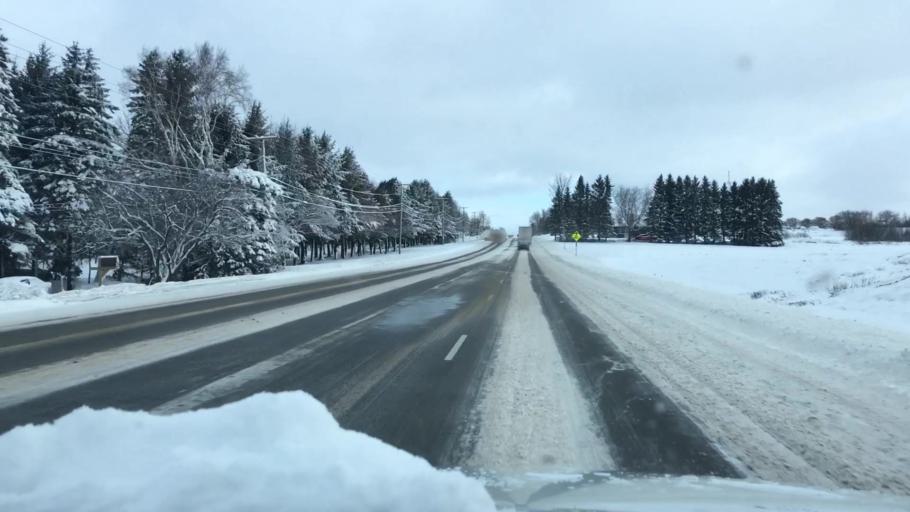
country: US
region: Maine
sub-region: Aroostook County
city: Presque Isle
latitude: 46.7219
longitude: -68.0060
